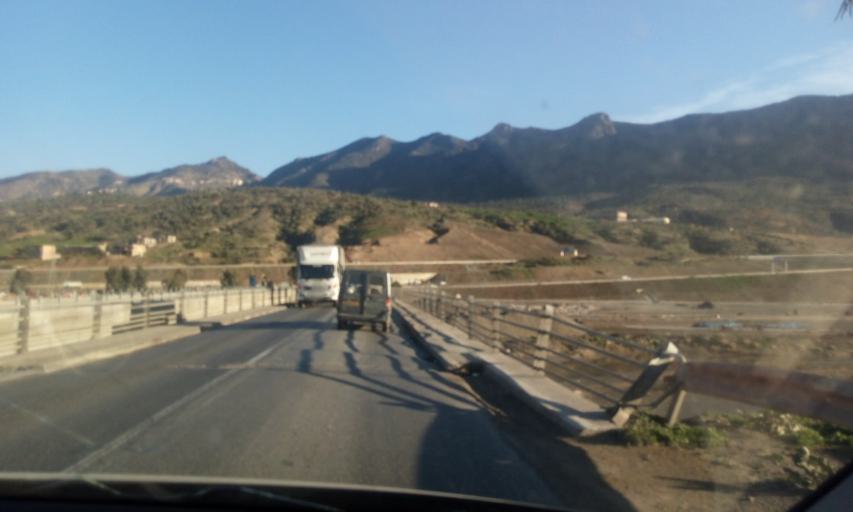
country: DZ
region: Bejaia
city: Akbou
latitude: 36.4820
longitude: 4.5908
